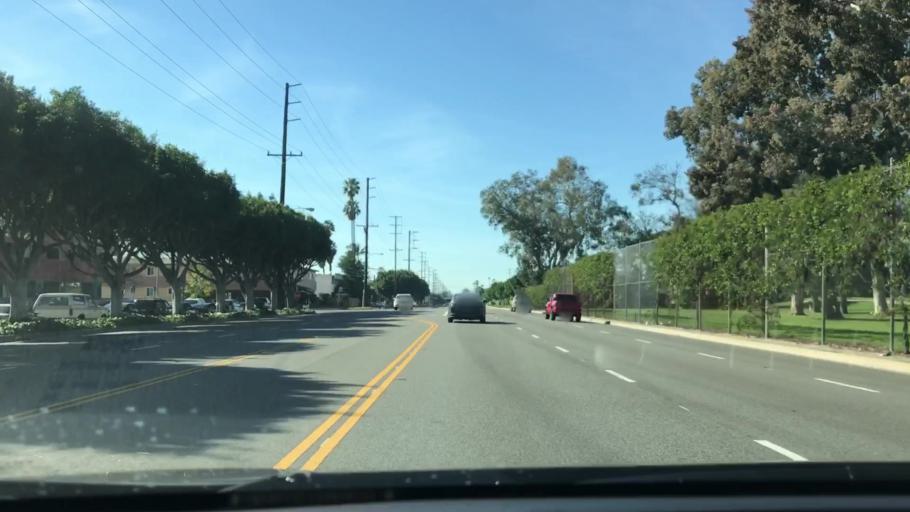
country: US
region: California
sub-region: Los Angeles County
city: West Athens
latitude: 33.9165
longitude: -118.3127
